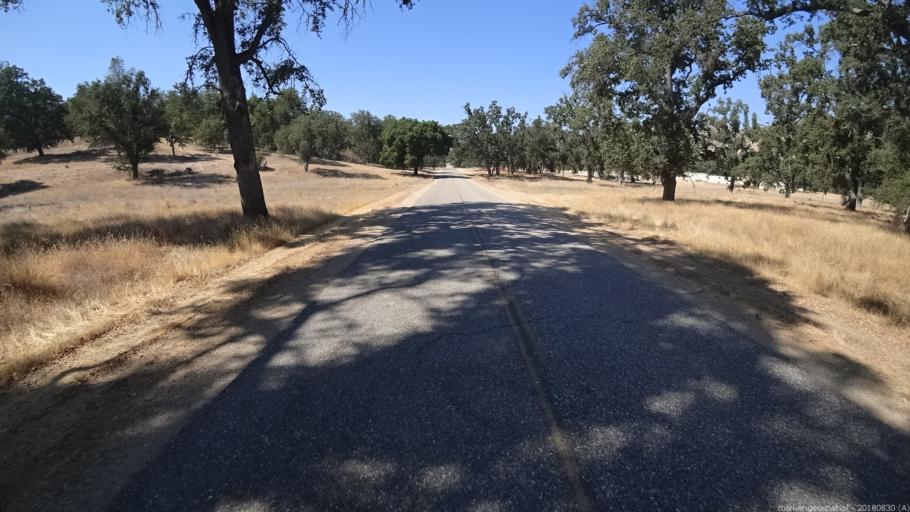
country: US
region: California
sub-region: Monterey County
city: King City
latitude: 36.0331
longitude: -121.2929
